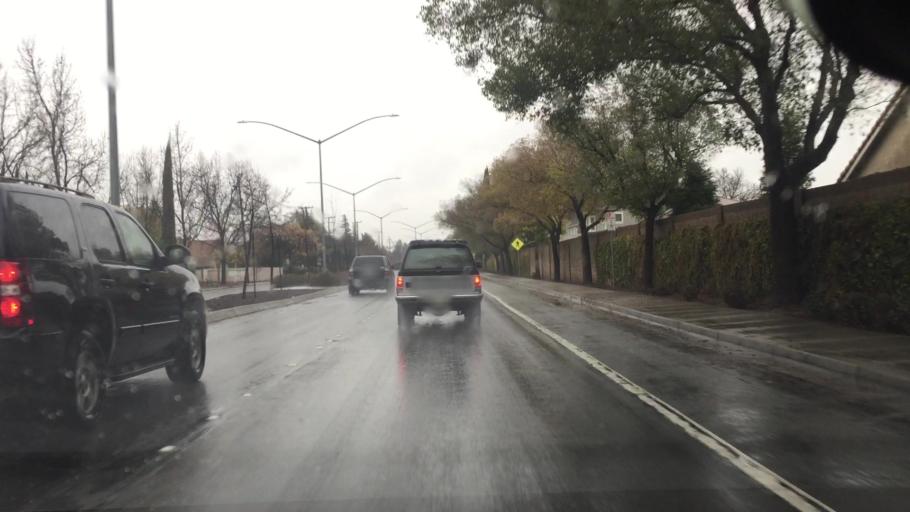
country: US
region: California
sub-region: San Joaquin County
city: Tracy
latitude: 37.7252
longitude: -121.4291
